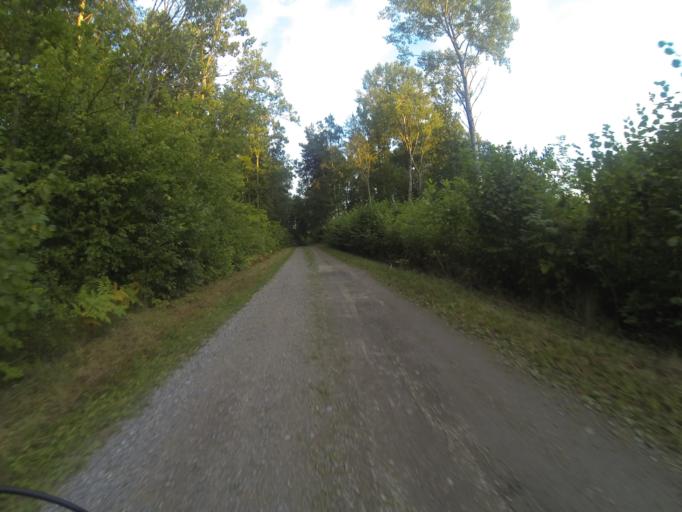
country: SE
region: Soedermanland
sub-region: Eskilstuna Kommun
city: Hallbybrunn
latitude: 59.4465
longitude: 16.3898
